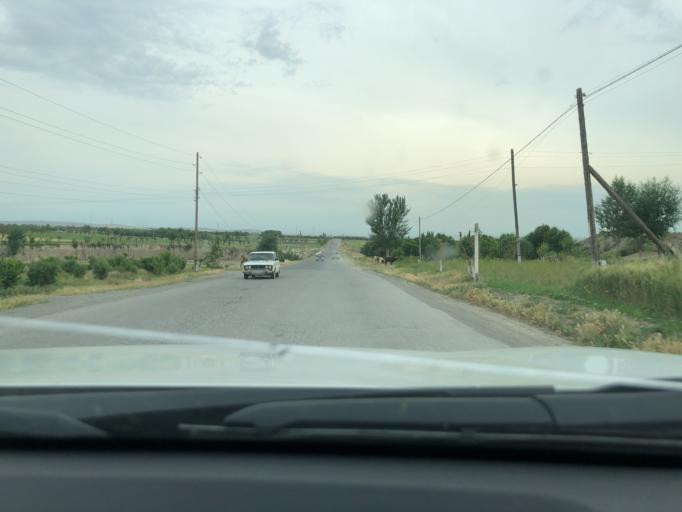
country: UZ
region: Toshkent
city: Bekobod
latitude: 40.1626
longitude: 69.2538
